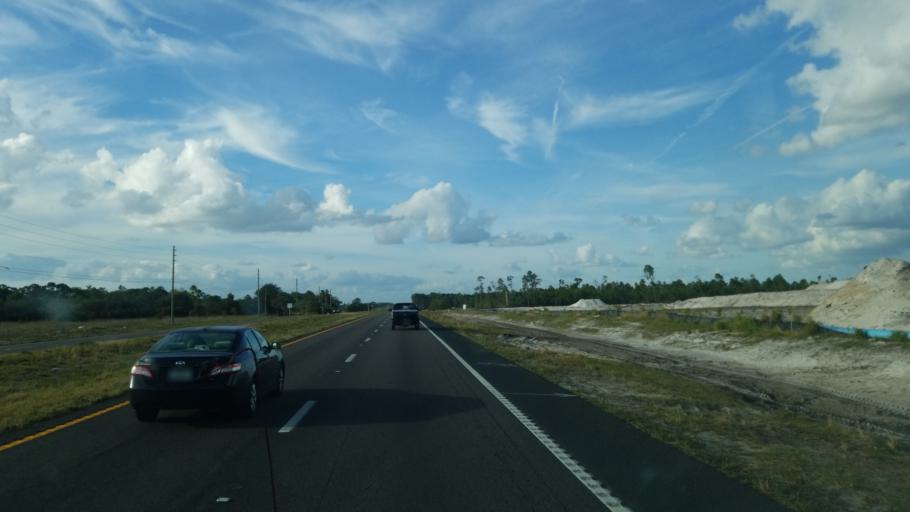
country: US
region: Florida
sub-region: Osceola County
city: Saint Cloud
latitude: 28.2225
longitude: -81.1805
